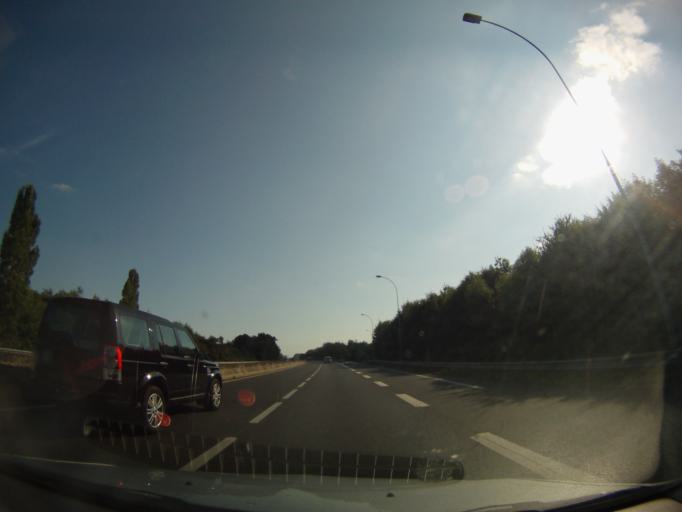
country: FR
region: Pays de la Loire
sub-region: Departement de la Loire-Atlantique
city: Carquefou
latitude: 47.2881
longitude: -1.5051
